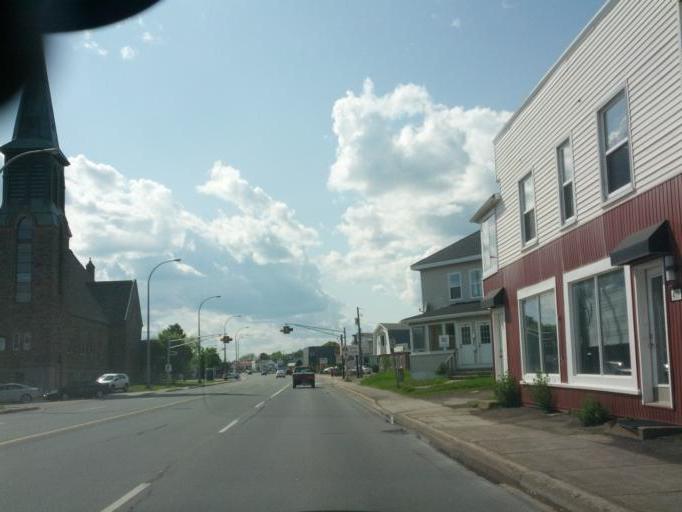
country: CA
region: New Brunswick
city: Moncton
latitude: 46.0971
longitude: -64.7946
